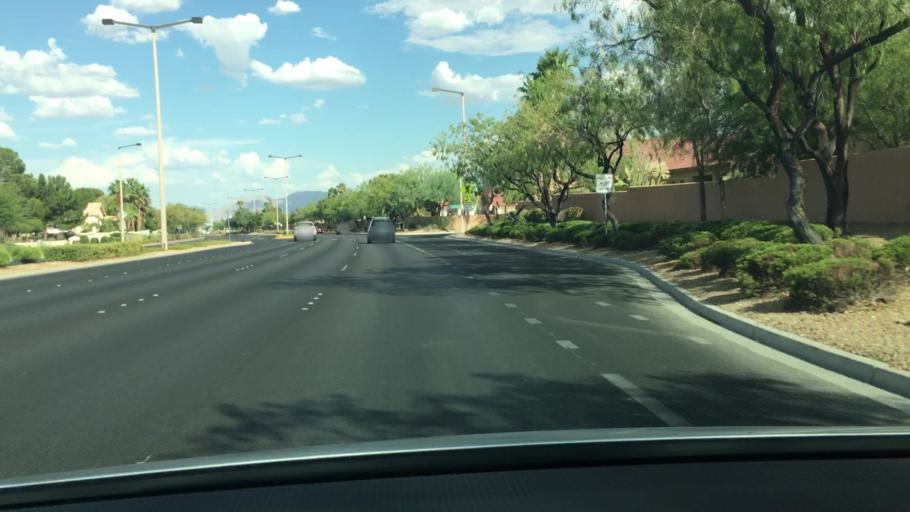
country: US
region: Nevada
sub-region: Clark County
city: Spring Valley
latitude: 36.1968
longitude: -115.2755
